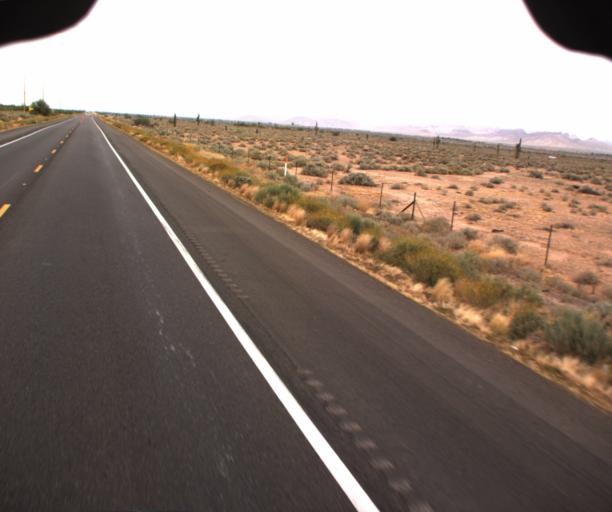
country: US
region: Arizona
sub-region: Pinal County
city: Blackwater
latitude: 33.0265
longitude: -111.6426
